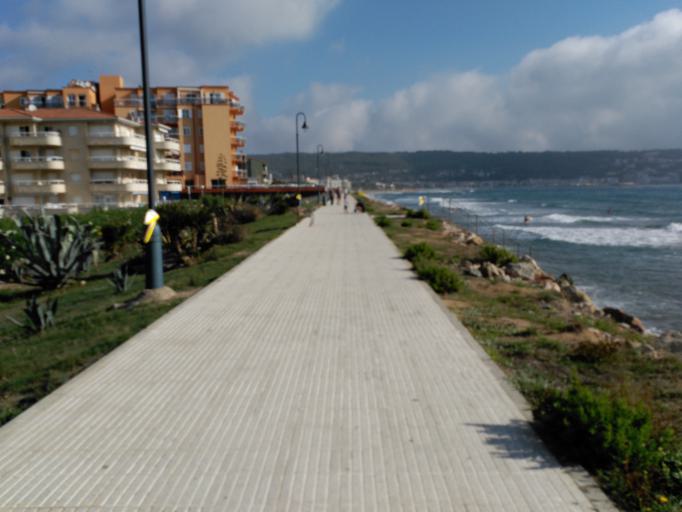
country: ES
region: Catalonia
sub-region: Provincia de Girona
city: Torroella de Montgri
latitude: 42.0414
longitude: 3.1961
